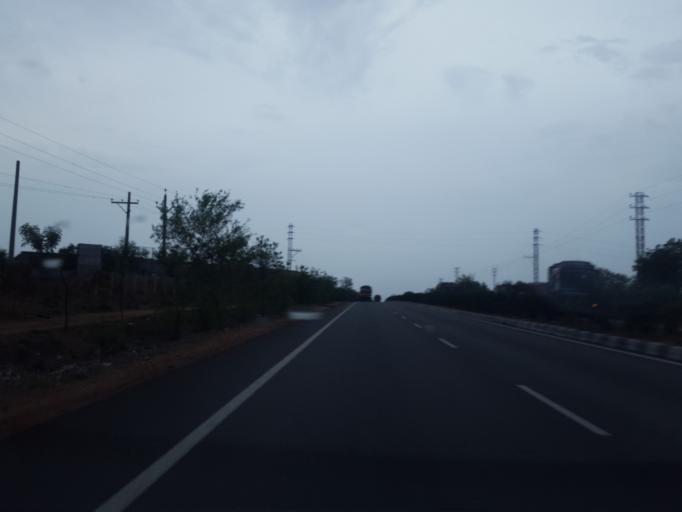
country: IN
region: Telangana
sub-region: Mahbubnagar
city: Farrukhnagar
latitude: 17.1294
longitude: 78.2798
